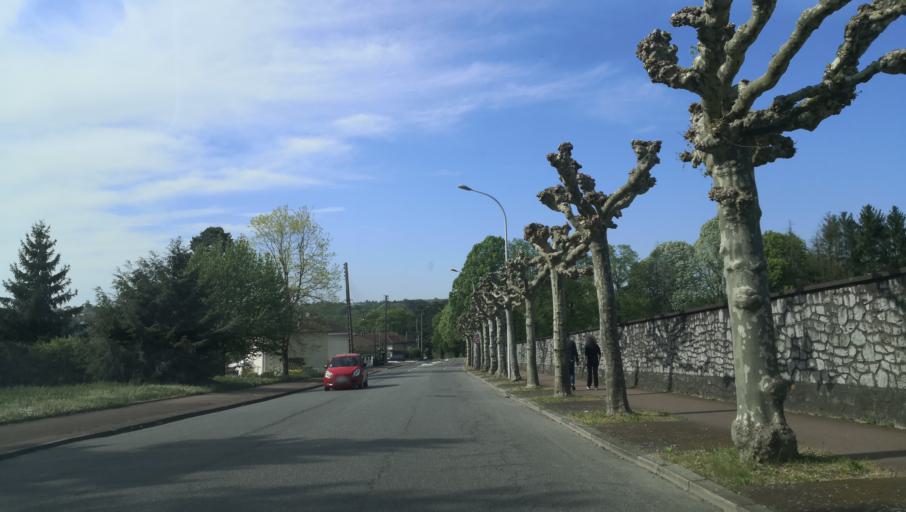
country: FR
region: Limousin
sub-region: Departement de la Haute-Vienne
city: Couzeix
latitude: 45.8573
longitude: 1.2586
